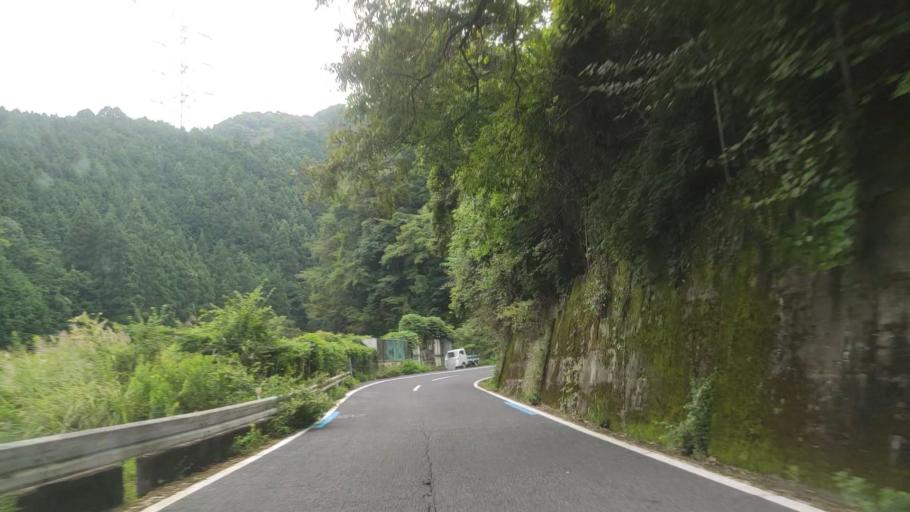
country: JP
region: Wakayama
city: Koya
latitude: 34.2390
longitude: 135.5472
